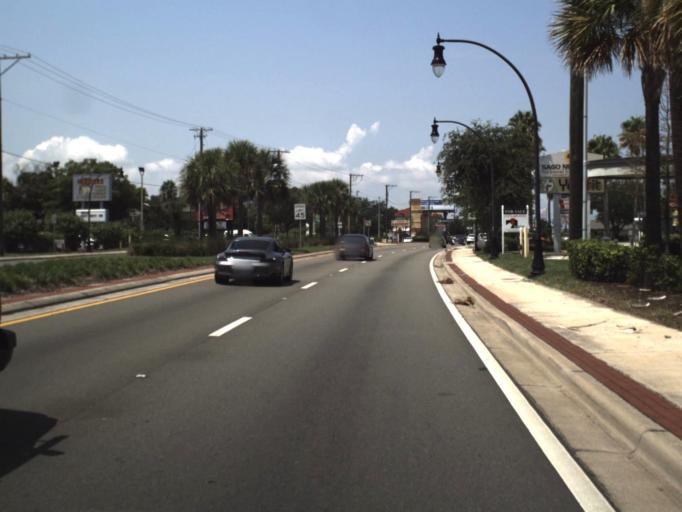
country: US
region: Florida
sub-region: Hillsborough County
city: Tampa
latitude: 27.8936
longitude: -82.5192
